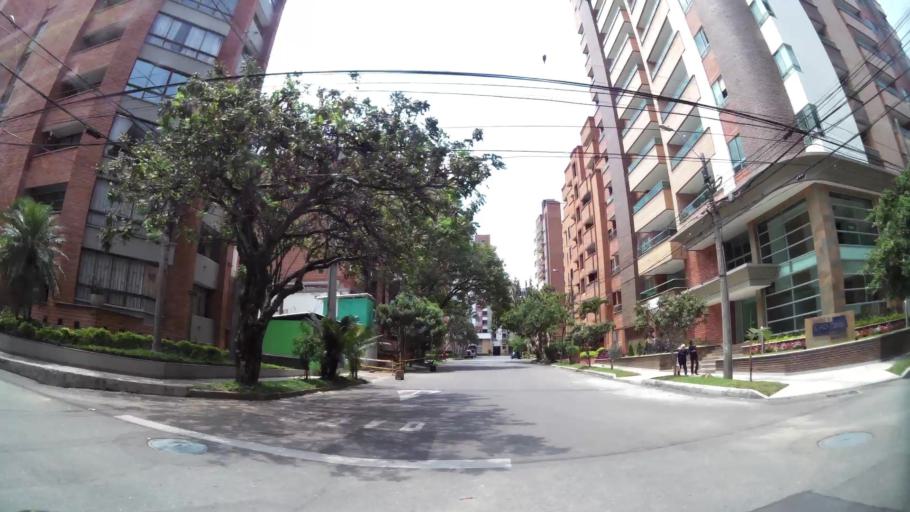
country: CO
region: Antioquia
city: Medellin
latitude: 6.2415
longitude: -75.5977
